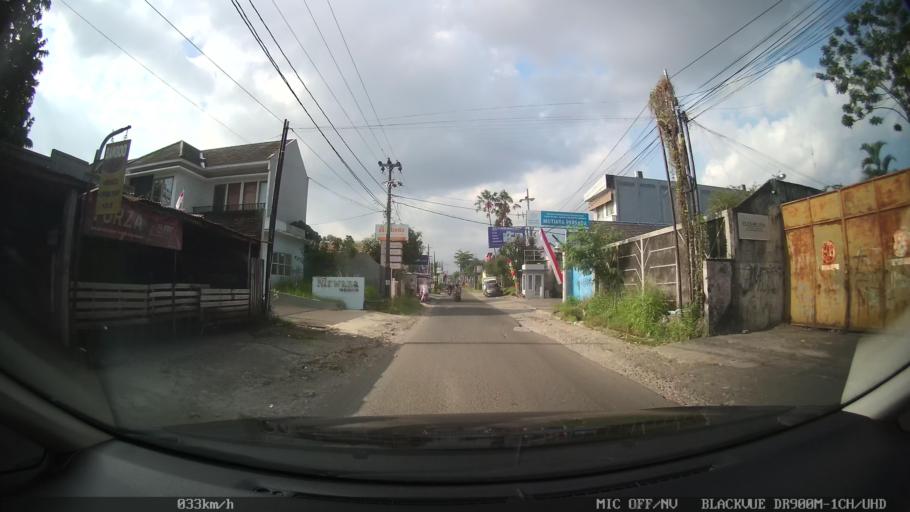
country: ID
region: Daerah Istimewa Yogyakarta
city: Yogyakarta
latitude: -7.7864
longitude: 110.3484
